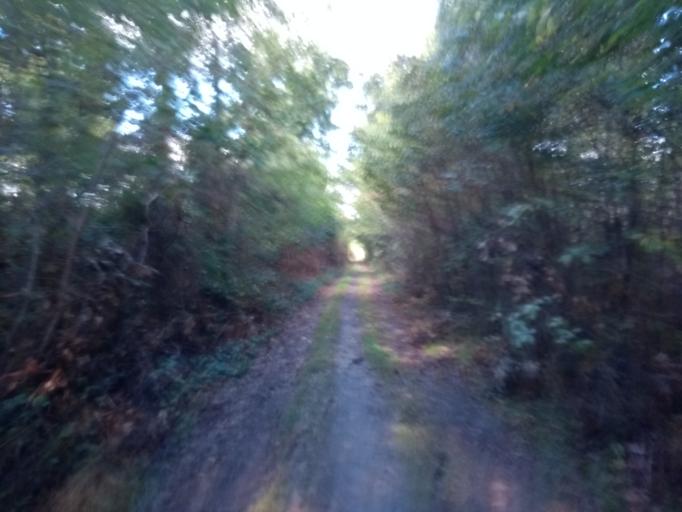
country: FR
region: Aquitaine
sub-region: Departement de la Gironde
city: Pessac
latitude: 44.8231
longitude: -0.6795
